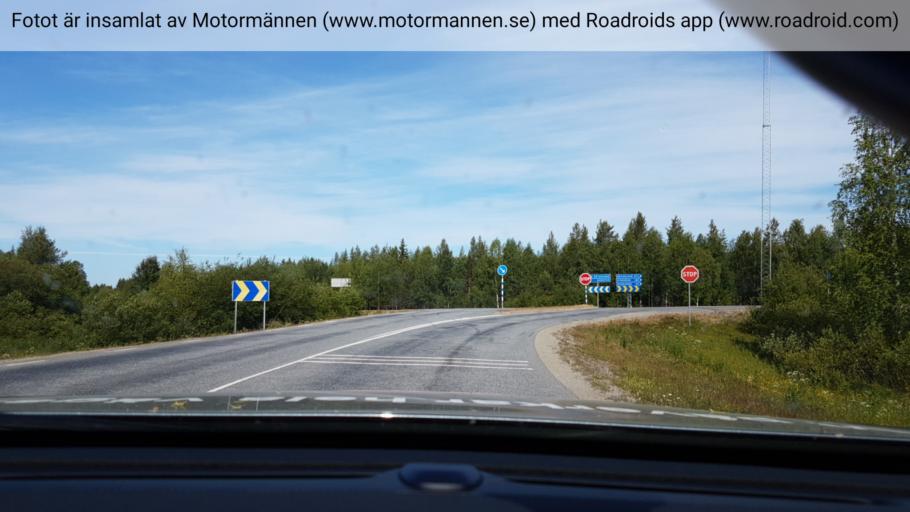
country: SE
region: Vaesterbotten
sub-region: Dorotea Kommun
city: Dorotea
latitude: 64.2532
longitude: 16.4808
